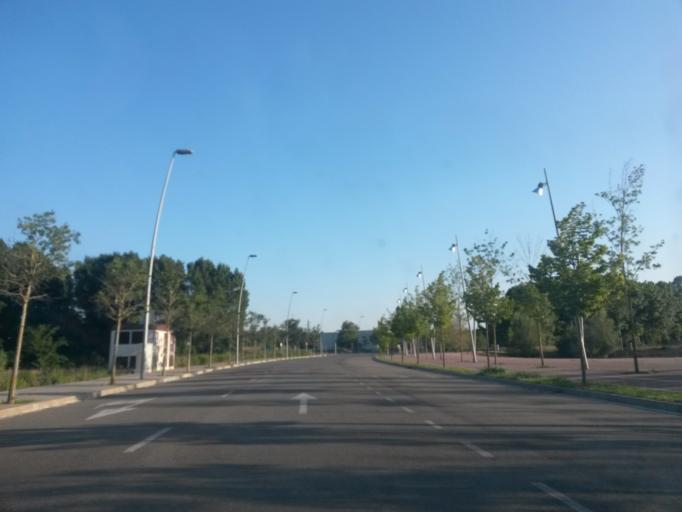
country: ES
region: Catalonia
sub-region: Provincia de Girona
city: Fornells de la Selva
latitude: 41.9493
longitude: 2.7994
